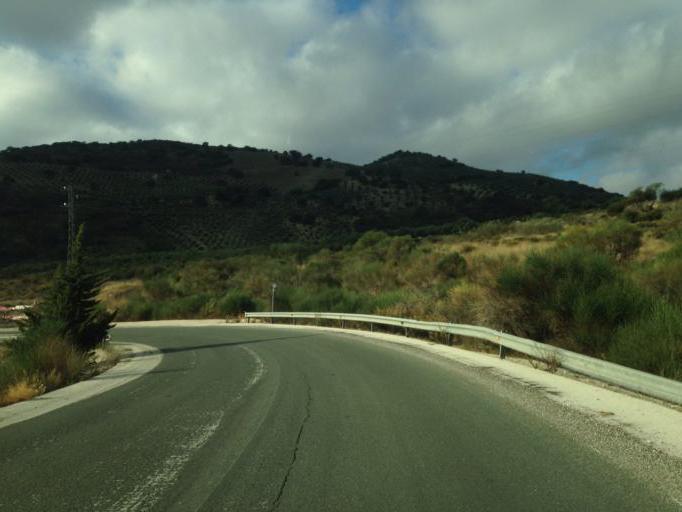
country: ES
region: Andalusia
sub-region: Provincia de Malaga
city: Casabermeja
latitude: 36.9570
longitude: -4.4483
